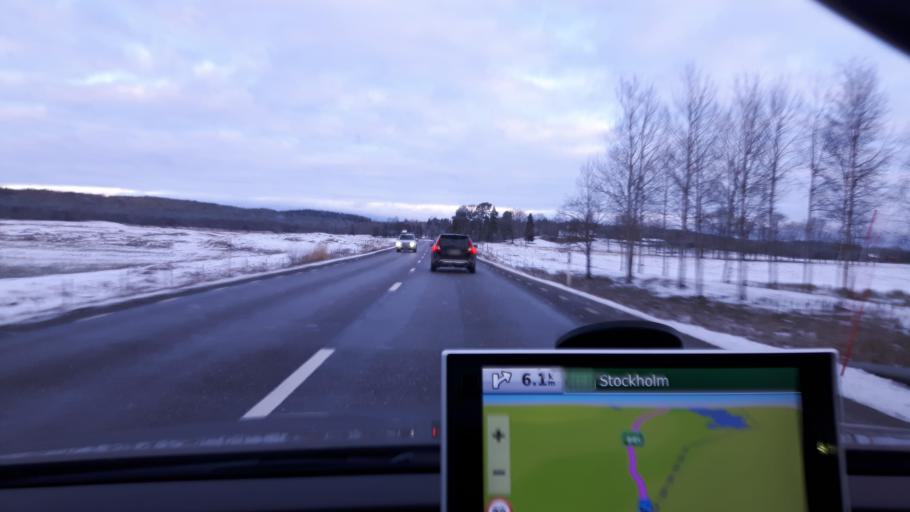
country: SE
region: Vaermland
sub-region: Saffle Kommun
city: Saeffle
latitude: 59.2072
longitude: 13.0263
